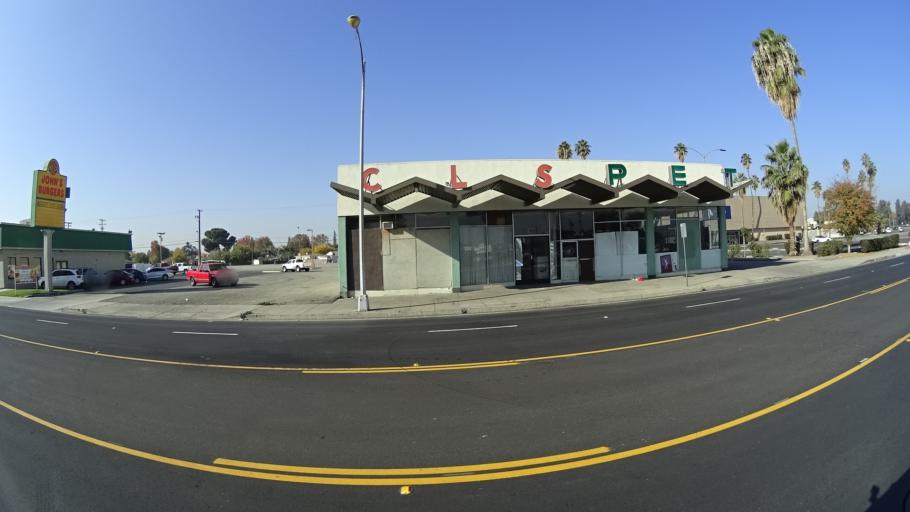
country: US
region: California
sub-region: Kern County
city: Bakersfield
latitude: 35.3879
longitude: -119.0235
